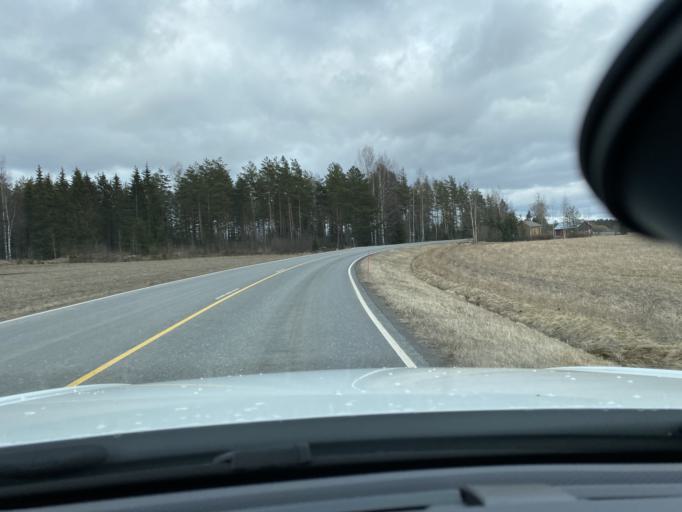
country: FI
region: Pirkanmaa
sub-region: Lounais-Pirkanmaa
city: Punkalaidun
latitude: 61.1041
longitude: 23.1617
